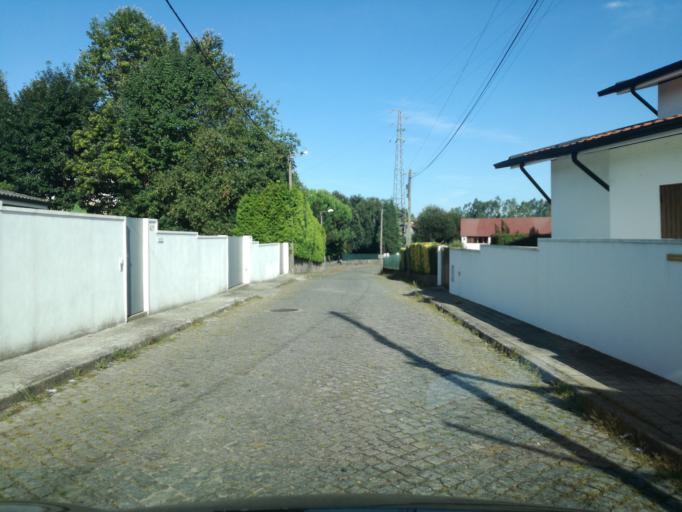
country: PT
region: Porto
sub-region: Maia
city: Nogueira
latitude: 41.2579
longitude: -8.5940
